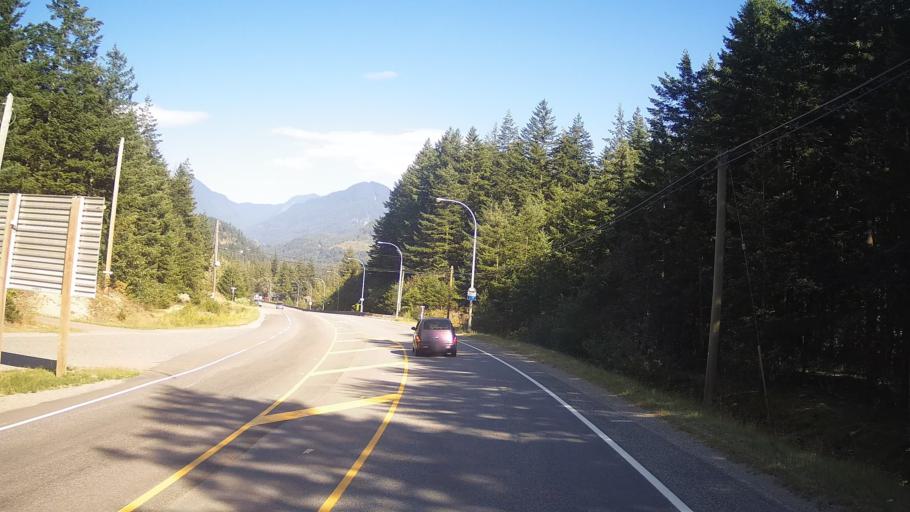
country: CA
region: British Columbia
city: Hope
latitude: 49.3863
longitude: -121.4588
